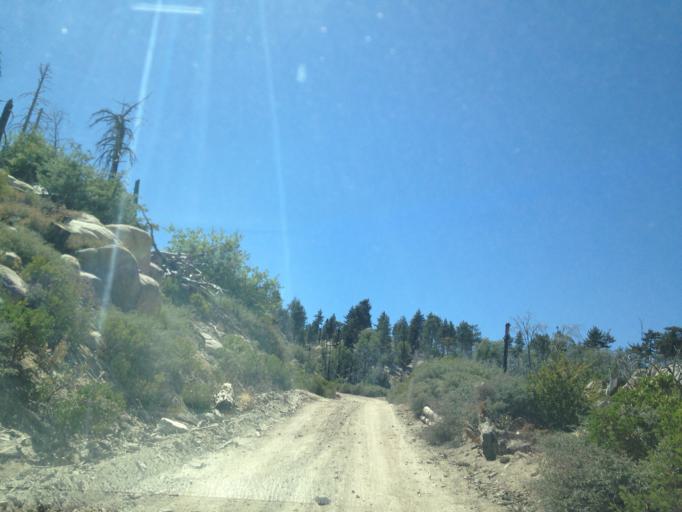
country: US
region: California
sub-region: San Bernardino County
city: Big Bear Lake
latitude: 34.2642
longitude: -116.9909
